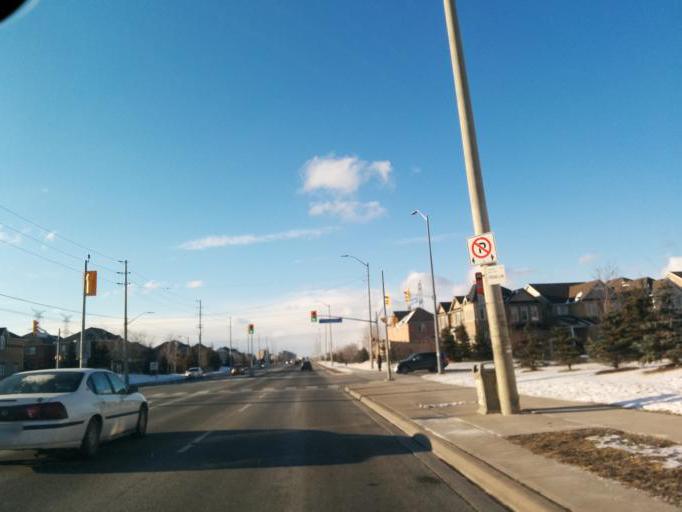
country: CA
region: Ontario
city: Brampton
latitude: 43.6411
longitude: -79.7227
